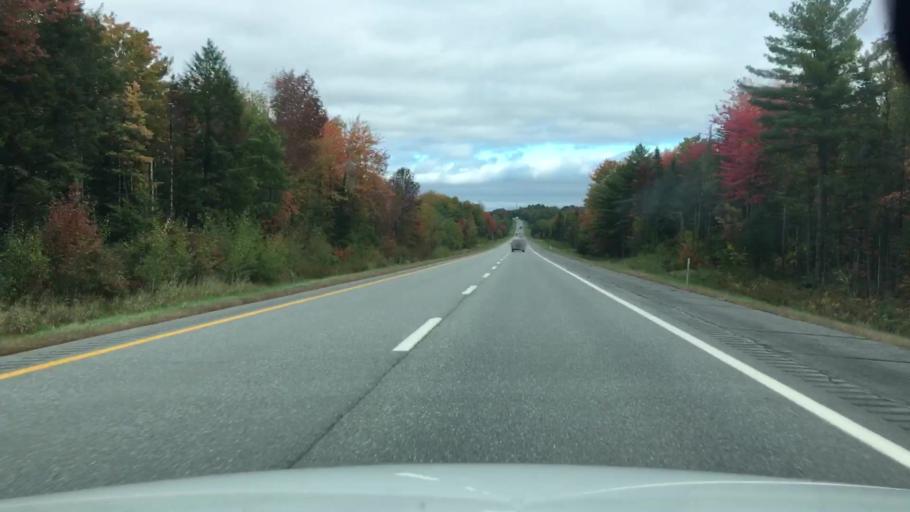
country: US
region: Maine
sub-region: Penobscot County
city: Carmel
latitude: 44.7771
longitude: -69.0551
